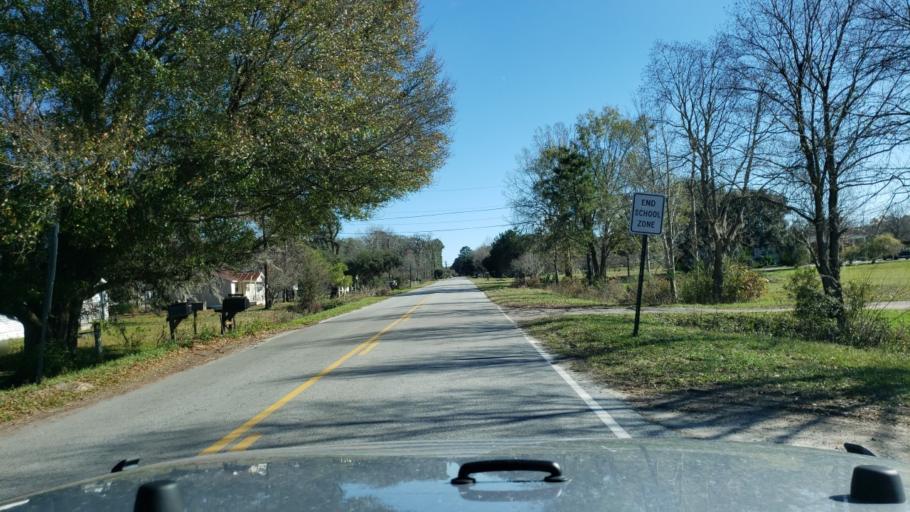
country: US
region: Georgia
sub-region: Chatham County
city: Georgetown
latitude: 32.0308
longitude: -81.1801
